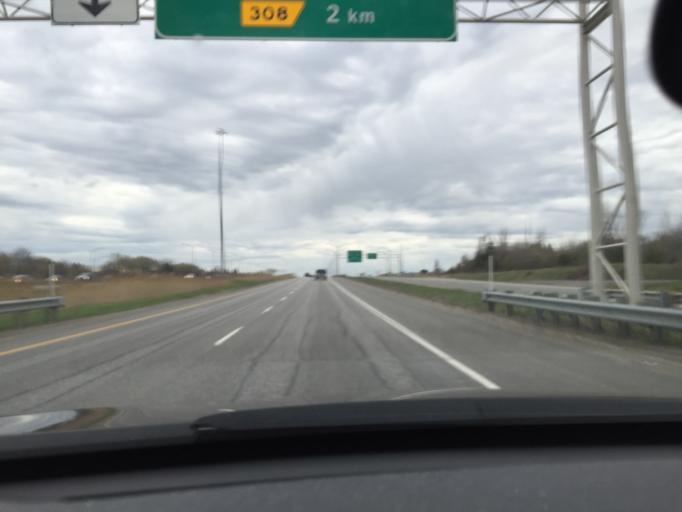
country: CA
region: Quebec
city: L'Ancienne-Lorette
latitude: 46.8236
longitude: -71.3026
